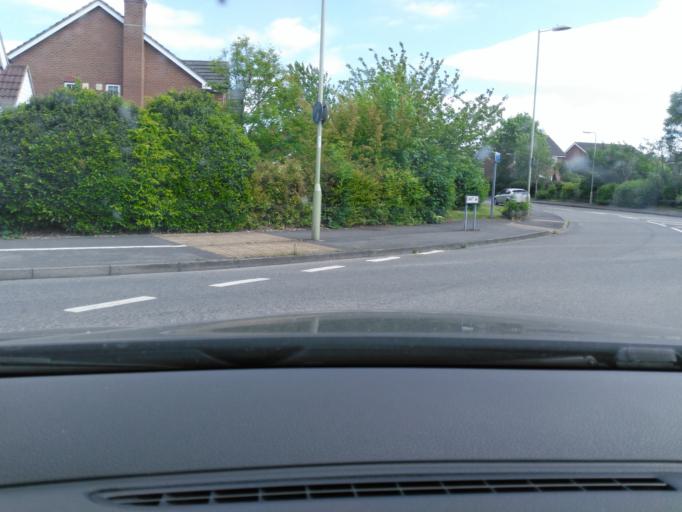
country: GB
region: England
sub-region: Hampshire
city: Andover
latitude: 51.2012
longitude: -1.5000
